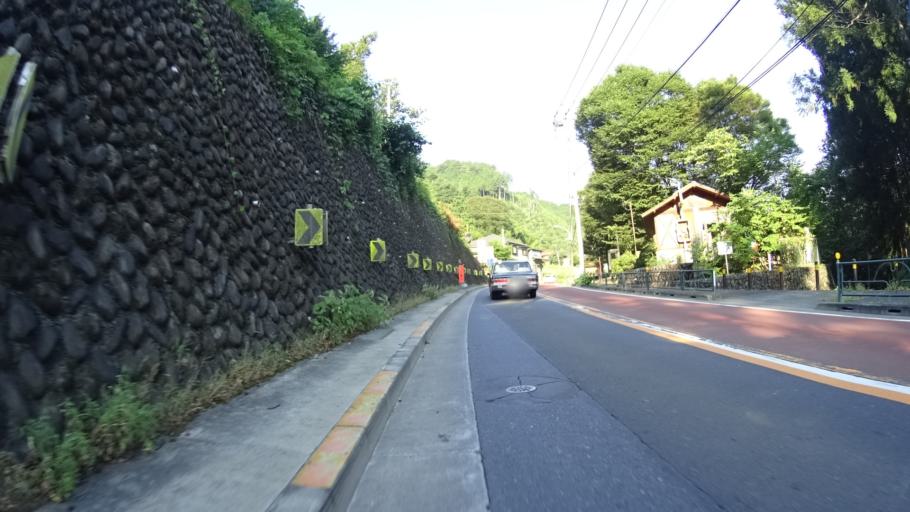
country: JP
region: Tokyo
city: Ome
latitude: 35.8027
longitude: 139.1961
